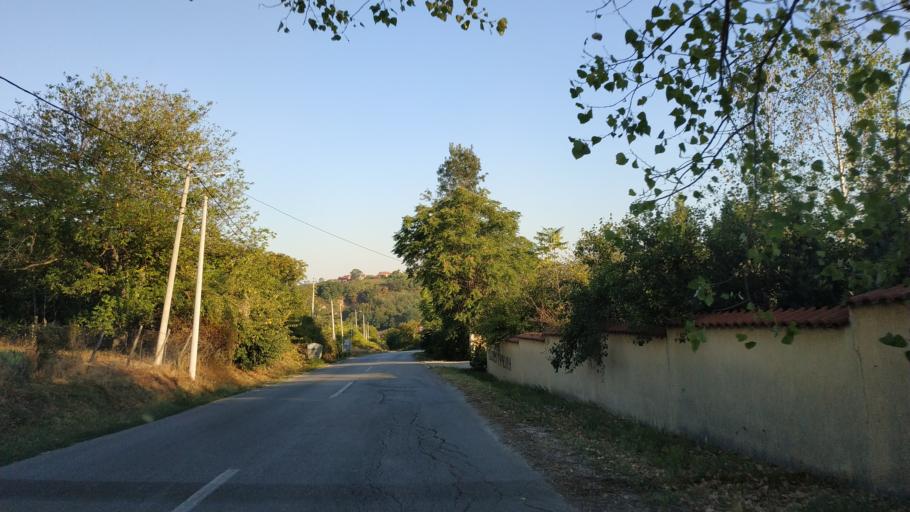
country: RS
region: Central Serbia
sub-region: Sumadijski Okrug
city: Topola
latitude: 44.2658
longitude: 20.6694
